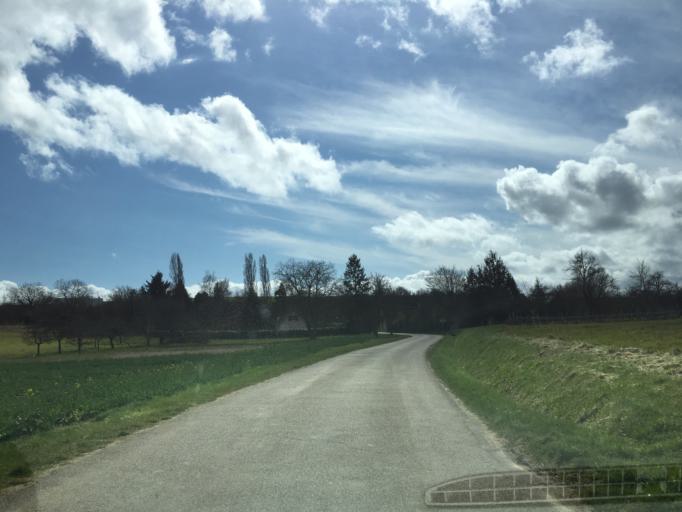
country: FR
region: Bourgogne
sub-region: Departement de l'Yonne
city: Pourrain
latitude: 47.7847
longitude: 3.4049
